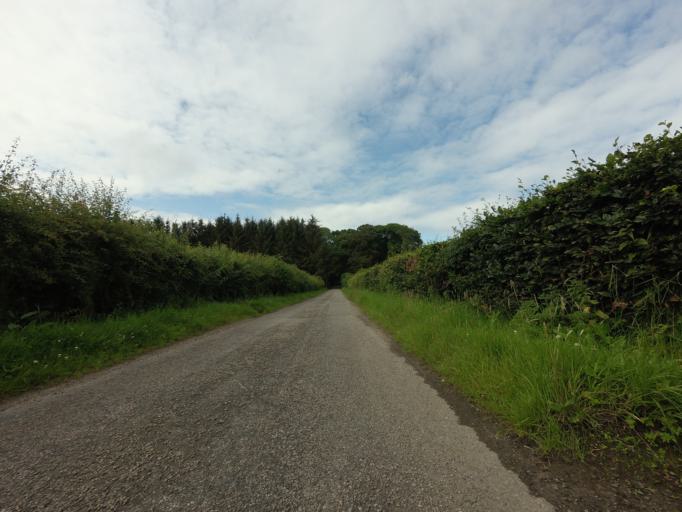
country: GB
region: Scotland
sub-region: Moray
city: Hopeman
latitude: 57.6726
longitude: -3.4102
